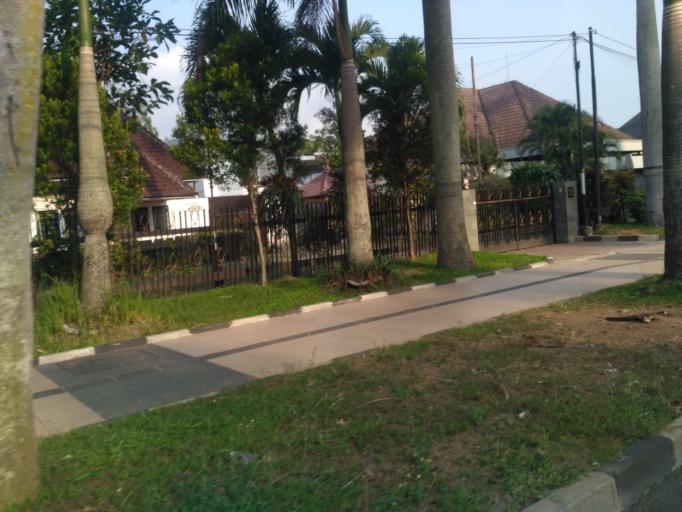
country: ID
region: East Java
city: Malang
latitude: -7.9695
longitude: 112.6233
